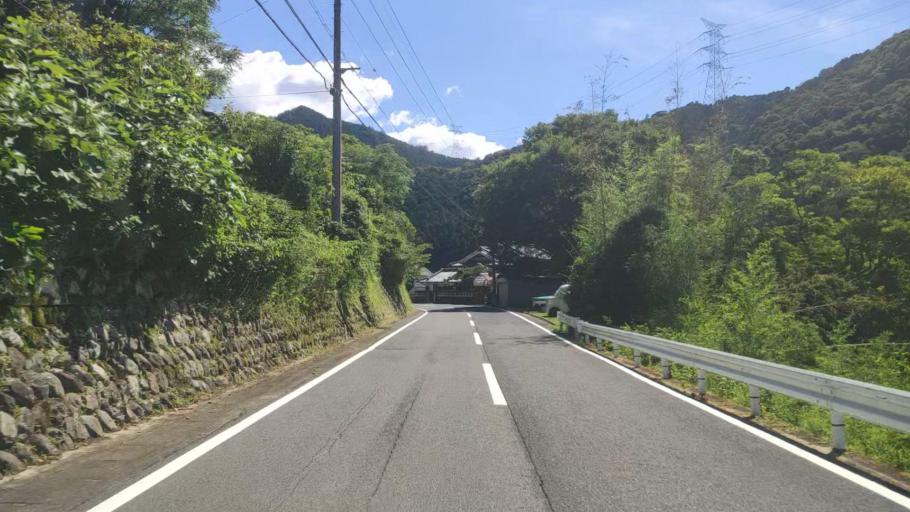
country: JP
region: Nara
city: Yoshino-cho
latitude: 34.3801
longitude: 135.9091
